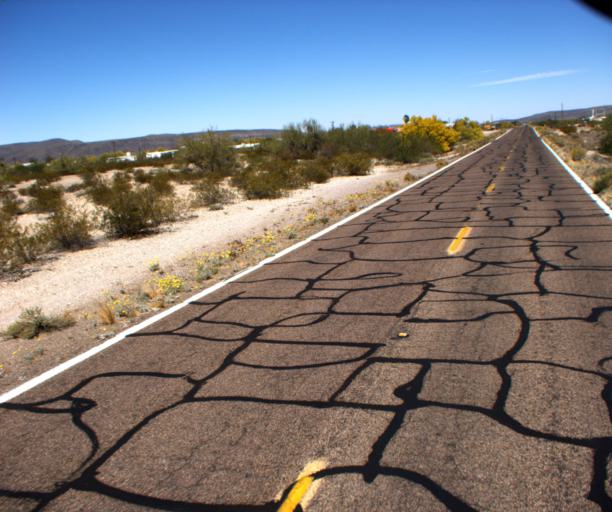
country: US
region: Arizona
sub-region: Pima County
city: Ajo
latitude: 32.4209
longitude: -112.8715
